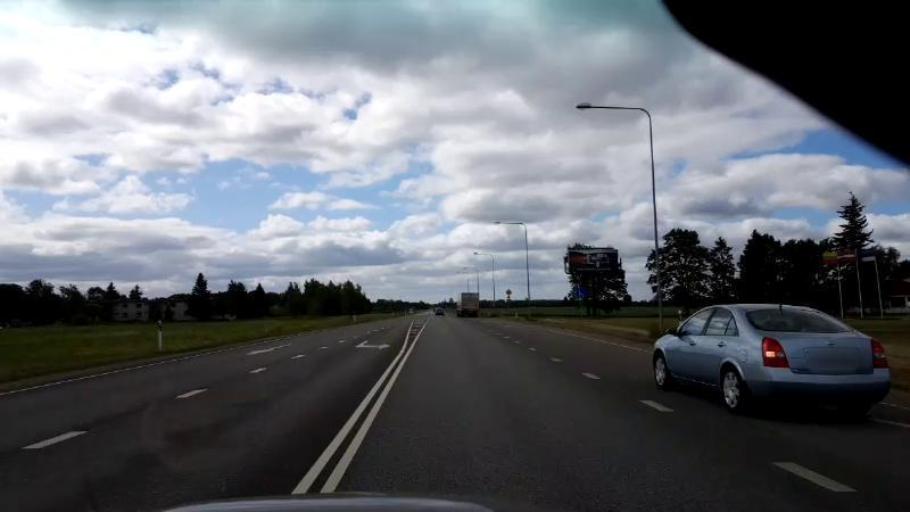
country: EE
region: Paernumaa
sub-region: Halinga vald
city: Parnu-Jaagupi
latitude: 58.5916
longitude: 24.5122
